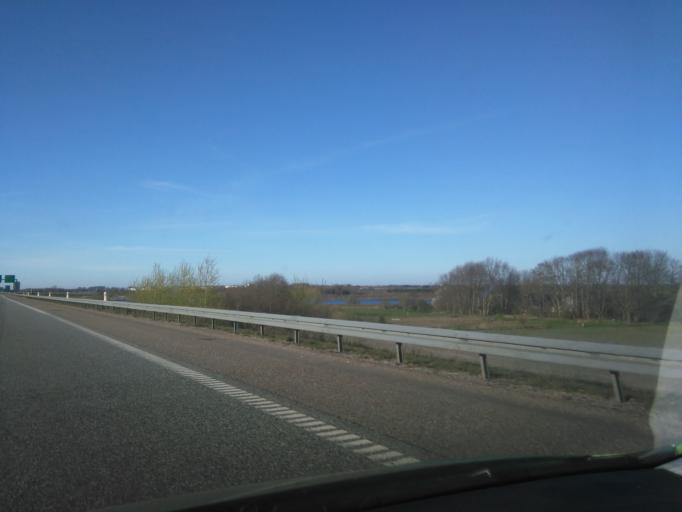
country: DK
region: Central Jutland
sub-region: Herning Kommune
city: Lind
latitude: 56.1125
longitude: 9.0105
